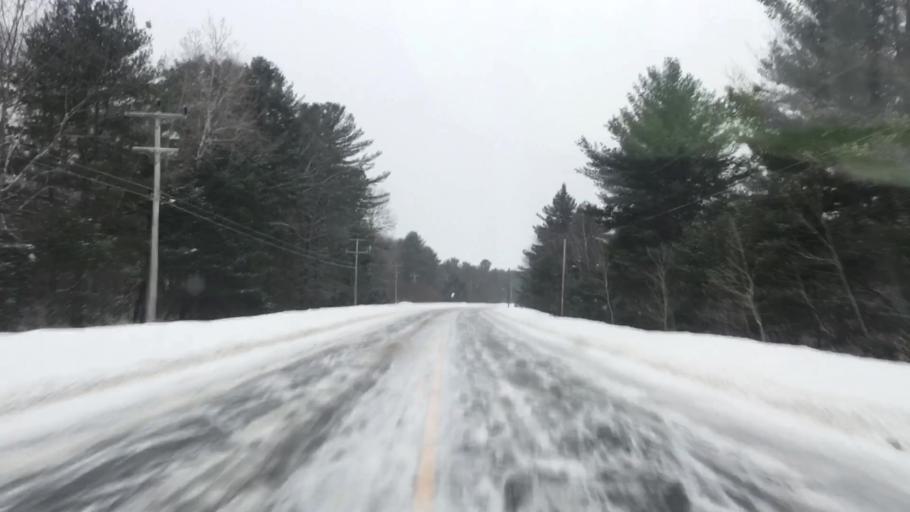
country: US
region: Maine
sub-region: Penobscot County
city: Medway
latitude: 45.5636
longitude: -68.3969
